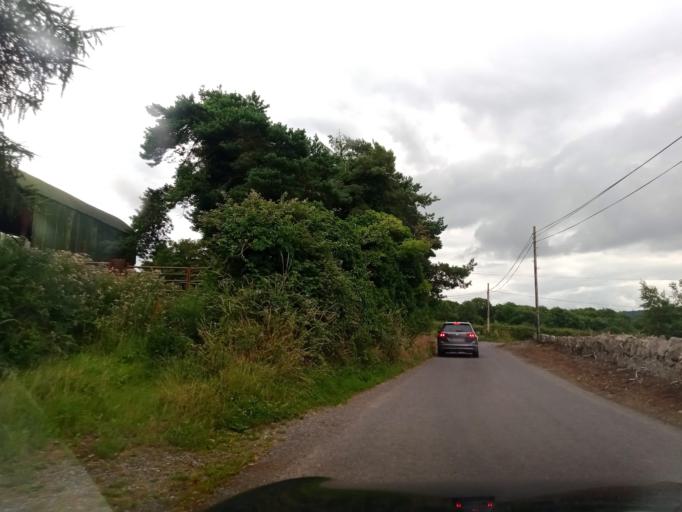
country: IE
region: Leinster
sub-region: Laois
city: Stradbally
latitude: 52.9674
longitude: -7.1430
